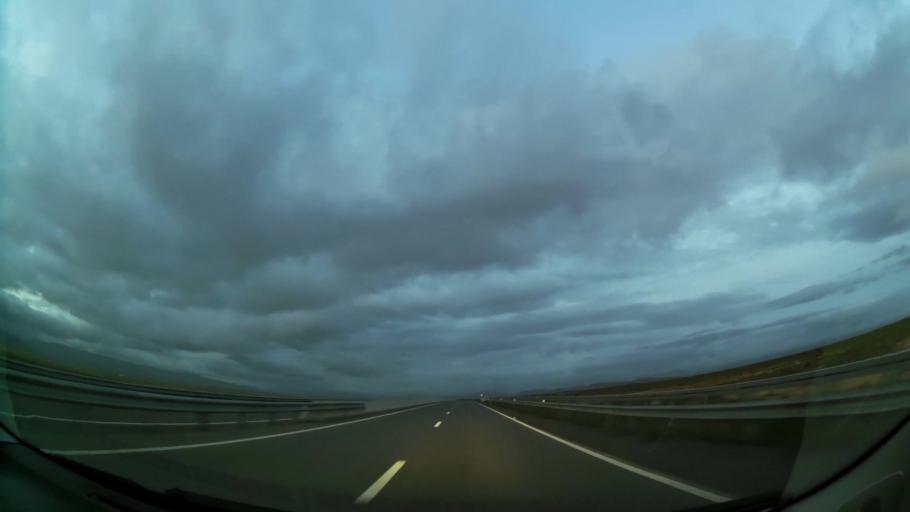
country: MA
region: Oriental
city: El Aioun
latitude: 34.6300
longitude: -2.3501
